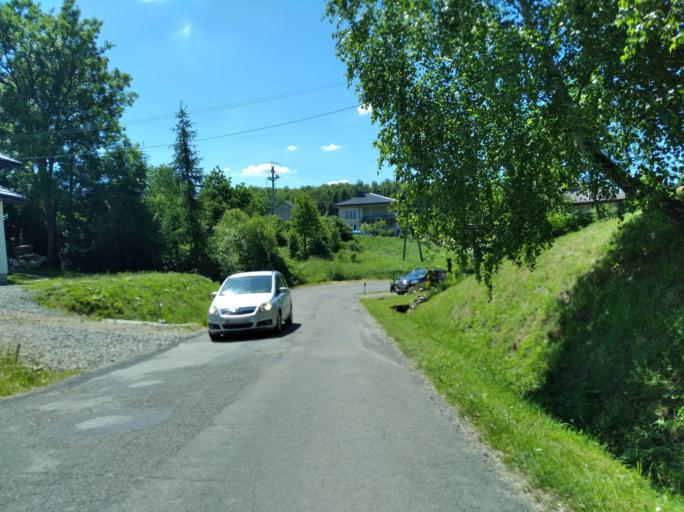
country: PL
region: Subcarpathian Voivodeship
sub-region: Powiat krosnienski
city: Chorkowka
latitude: 49.6387
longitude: 21.6108
